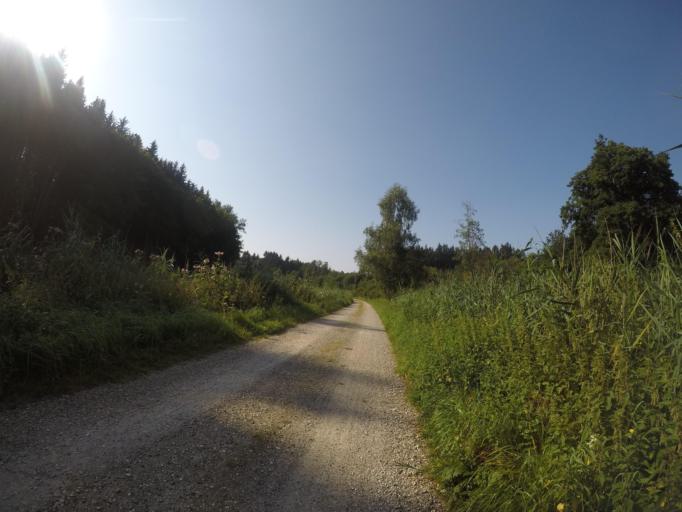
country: DE
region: Baden-Wuerttemberg
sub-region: Tuebingen Region
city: Schnurpflingen
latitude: 48.2539
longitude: 10.0069
